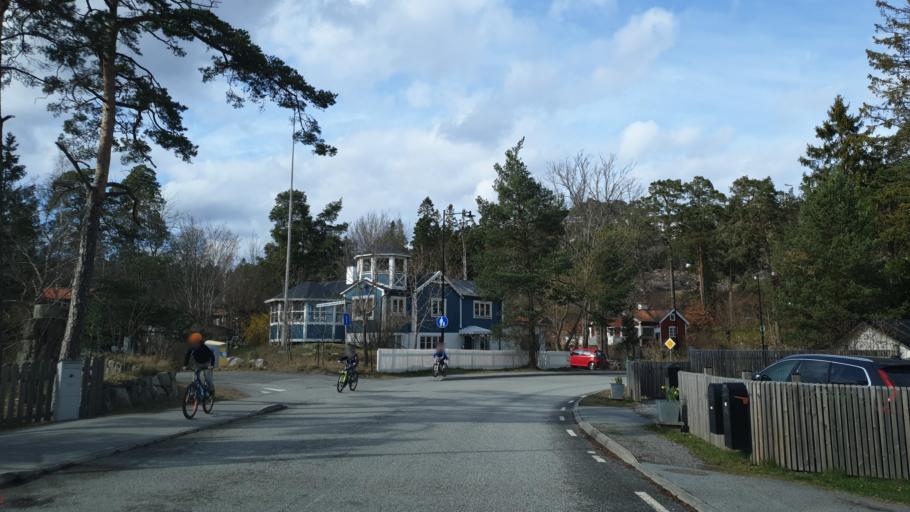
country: SE
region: Stockholm
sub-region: Nacka Kommun
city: Saltsjobaden
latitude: 59.2620
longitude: 18.3454
